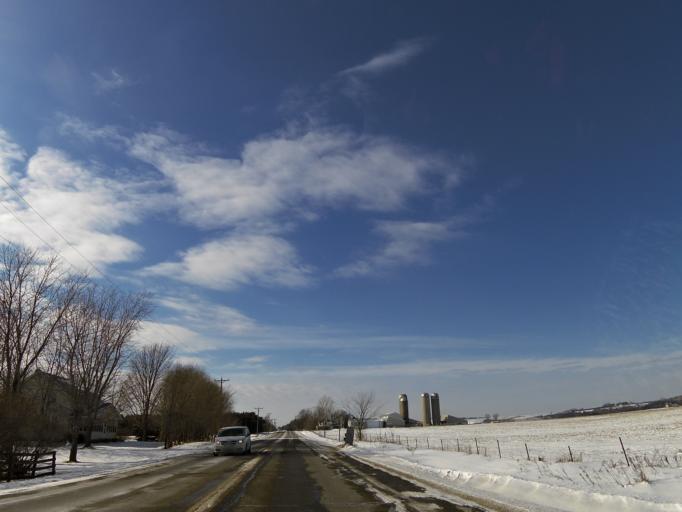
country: US
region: Wisconsin
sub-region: Saint Croix County
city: Roberts
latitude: 44.9926
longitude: -92.5633
